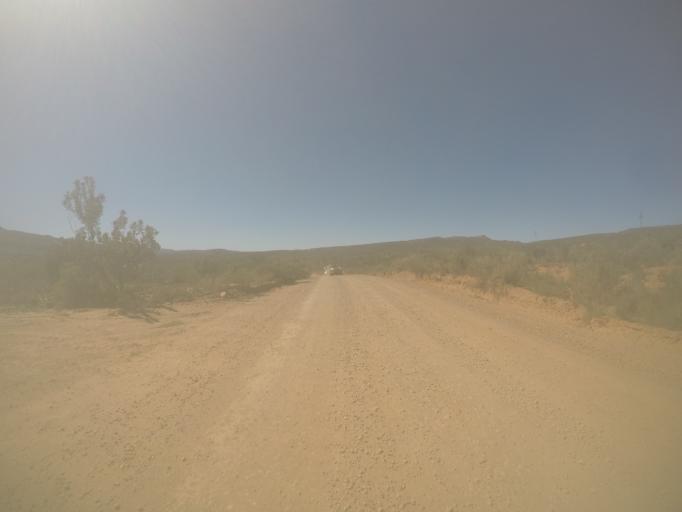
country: ZA
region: Western Cape
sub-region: West Coast District Municipality
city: Clanwilliam
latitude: -32.5006
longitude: 19.2776
